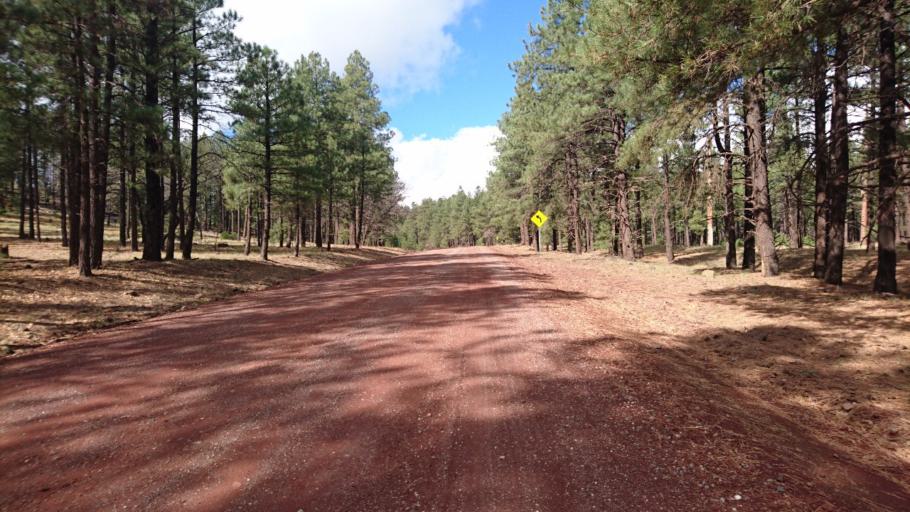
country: US
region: Arizona
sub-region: Coconino County
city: Parks
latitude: 35.2746
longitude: -111.8975
